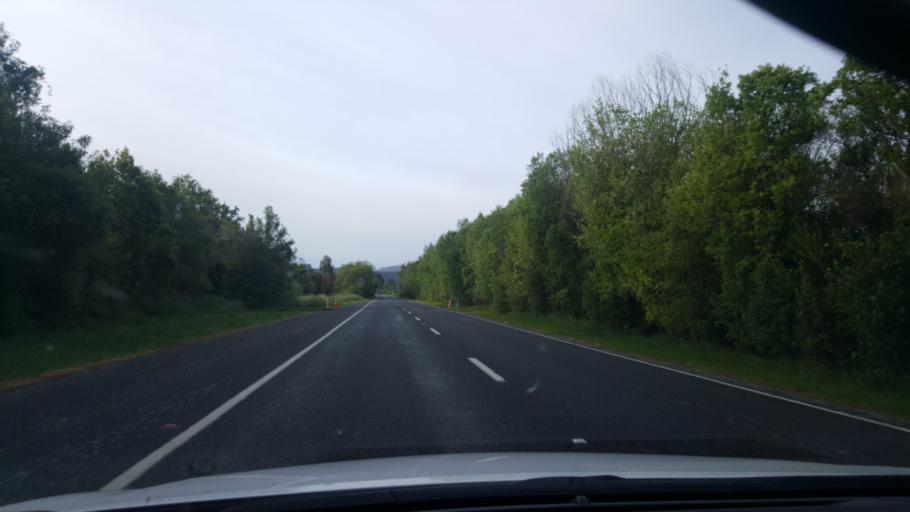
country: NZ
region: Waikato
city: Turangi
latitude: -38.9686
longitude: 175.7686
